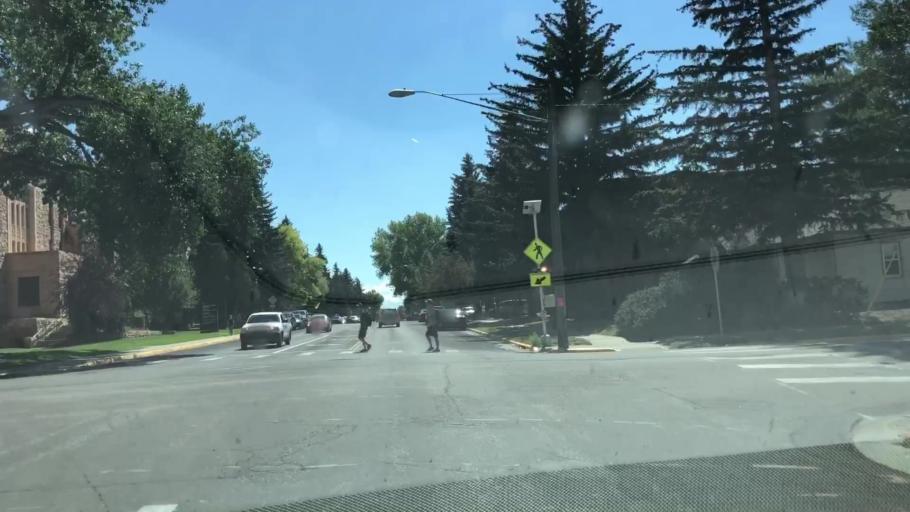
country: US
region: Wyoming
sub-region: Albany County
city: Laramie
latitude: 41.3154
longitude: -105.5853
